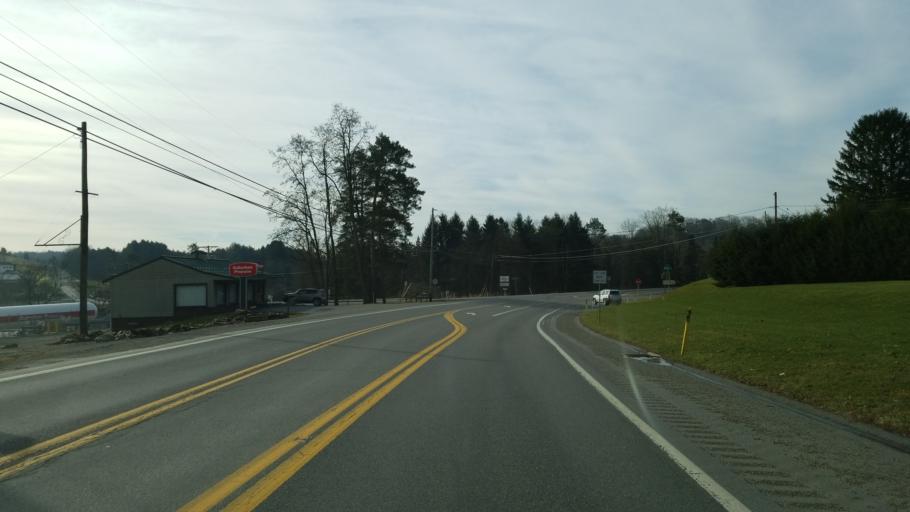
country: US
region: Pennsylvania
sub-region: Jefferson County
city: Albion
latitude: 40.9567
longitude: -78.9236
